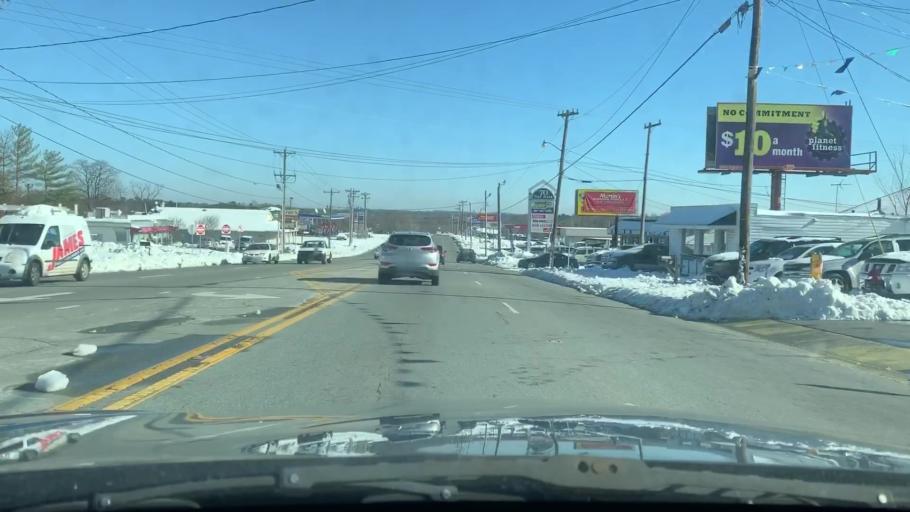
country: US
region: North Carolina
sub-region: Alamance County
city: Haw River
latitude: 36.0908
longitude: -79.3851
